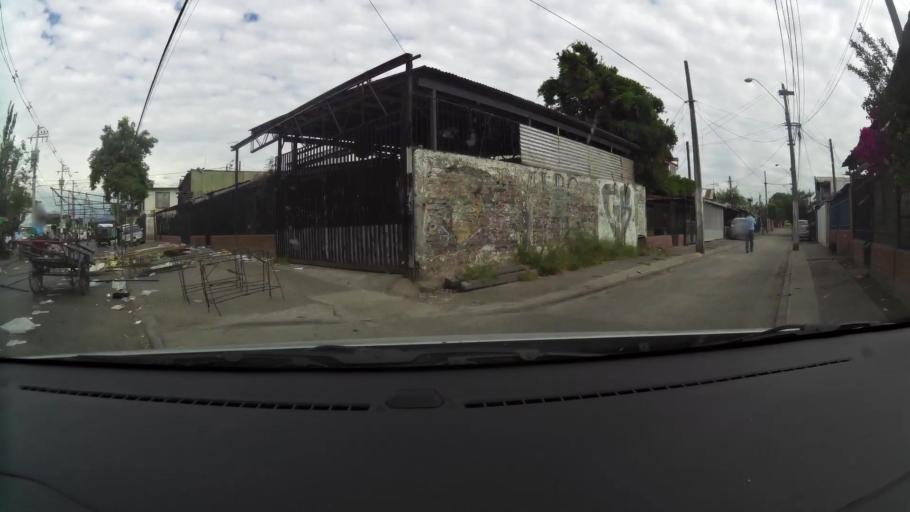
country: CL
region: Santiago Metropolitan
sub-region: Provincia de Santiago
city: La Pintana
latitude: -33.5809
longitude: -70.6366
